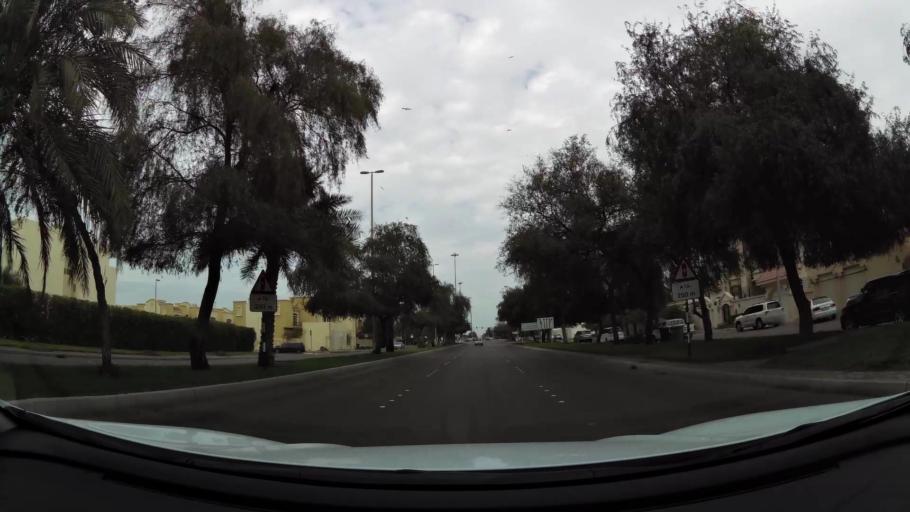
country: AE
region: Abu Dhabi
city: Abu Dhabi
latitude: 24.4342
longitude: 54.4037
